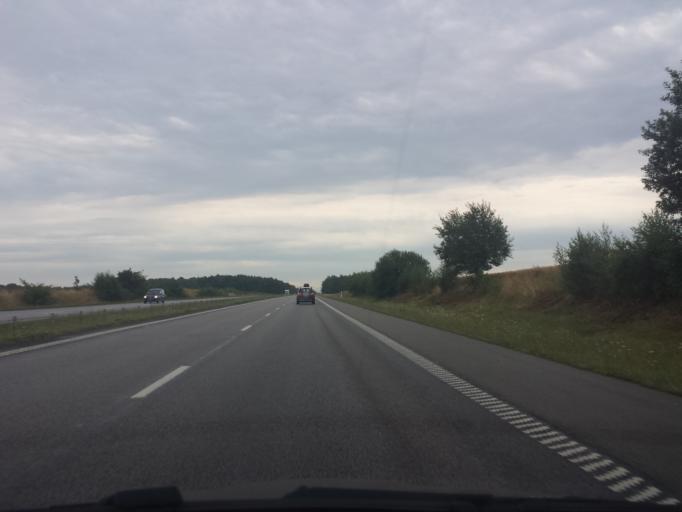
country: SE
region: Skane
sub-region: Malmo
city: Oxie
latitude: 55.5489
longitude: 13.1313
